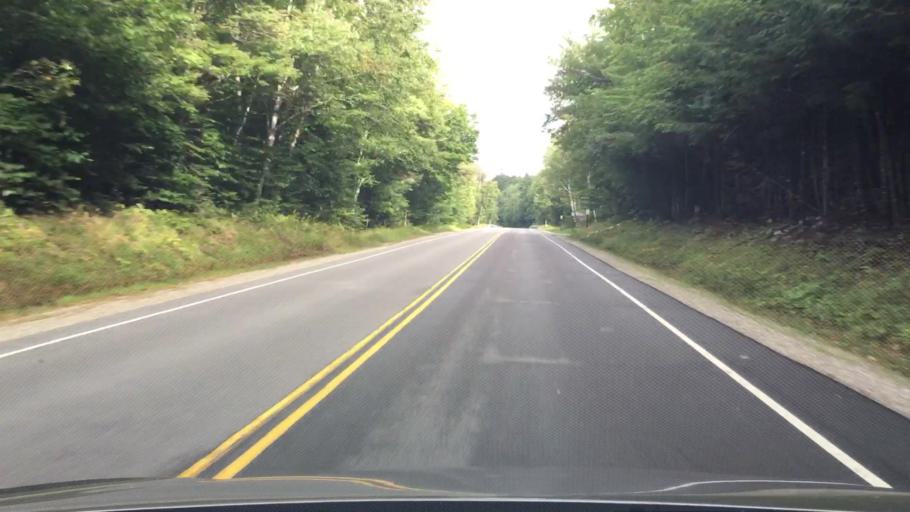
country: US
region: New Hampshire
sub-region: Carroll County
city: Tamworth
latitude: 43.9978
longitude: -71.3945
